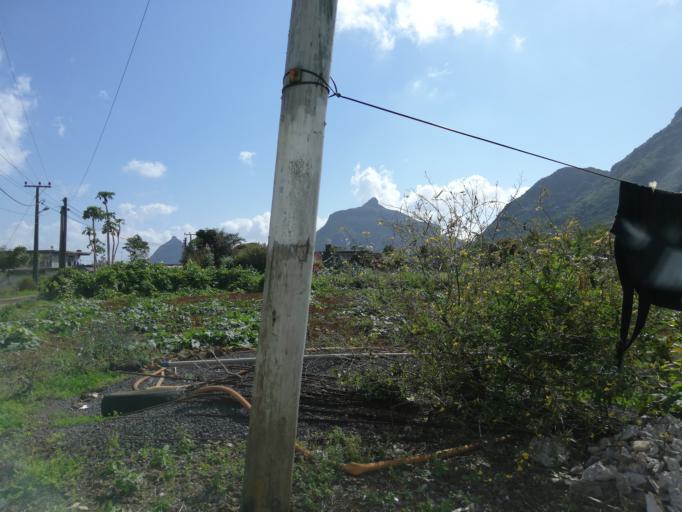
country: MU
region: Pamplemousses
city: Creve Coeur
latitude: -20.2030
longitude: 57.5546
